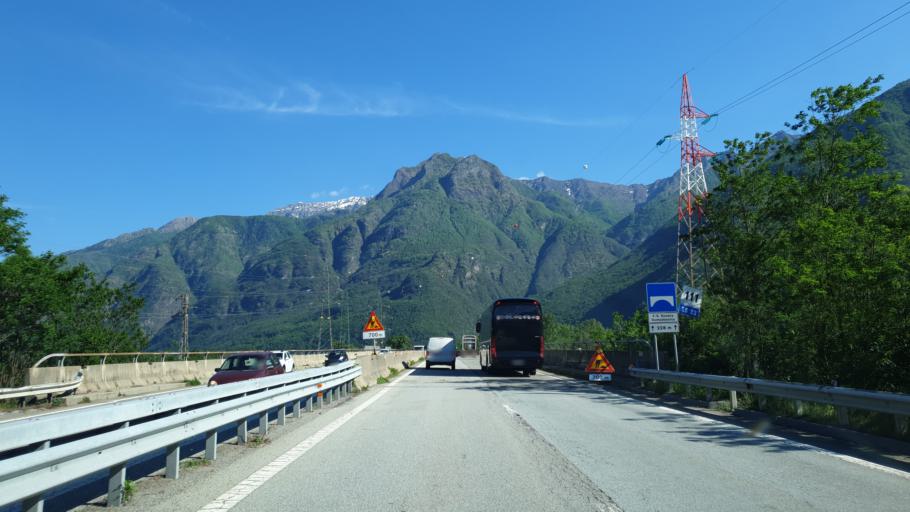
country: IT
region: Piedmont
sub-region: Provincia Verbano-Cusio-Ossola
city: Vogogna
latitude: 46.0108
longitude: 8.2789
